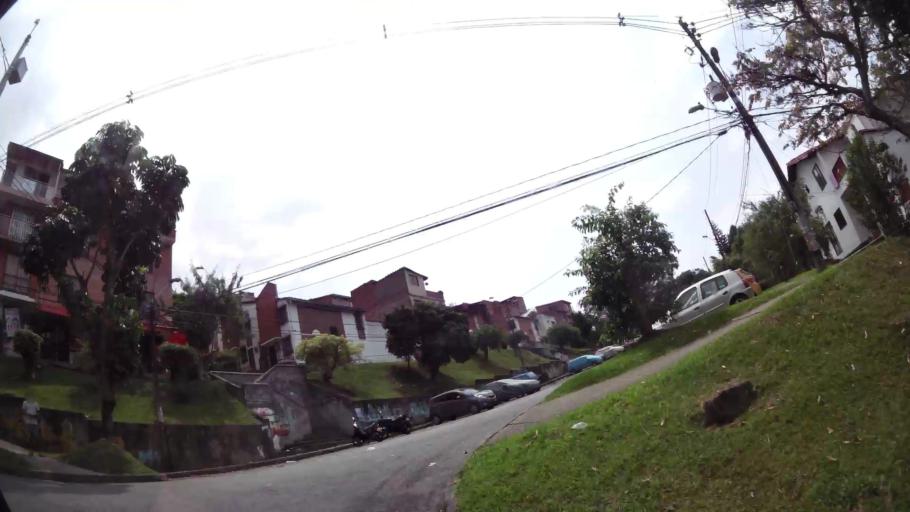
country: CO
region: Antioquia
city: Medellin
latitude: 6.2310
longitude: -75.5456
